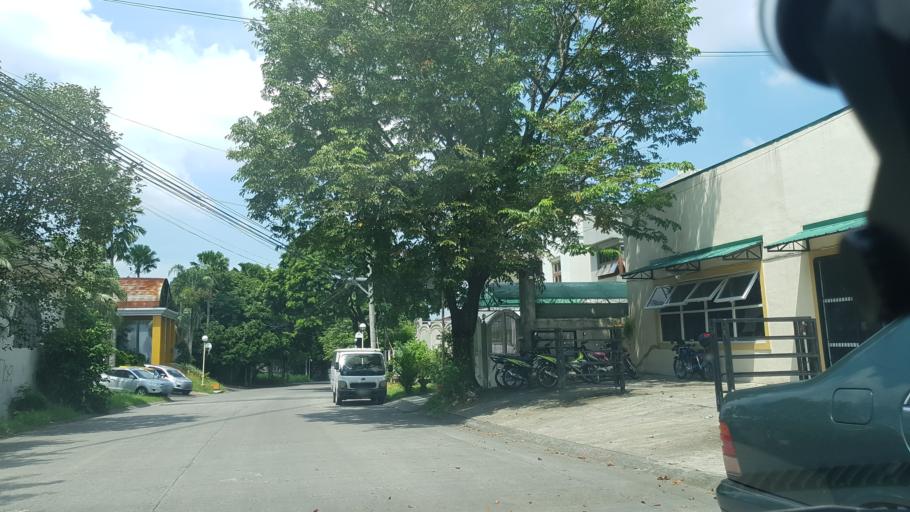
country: PH
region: Calabarzon
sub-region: Province of Rizal
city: Las Pinas
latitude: 14.4266
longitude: 120.9910
